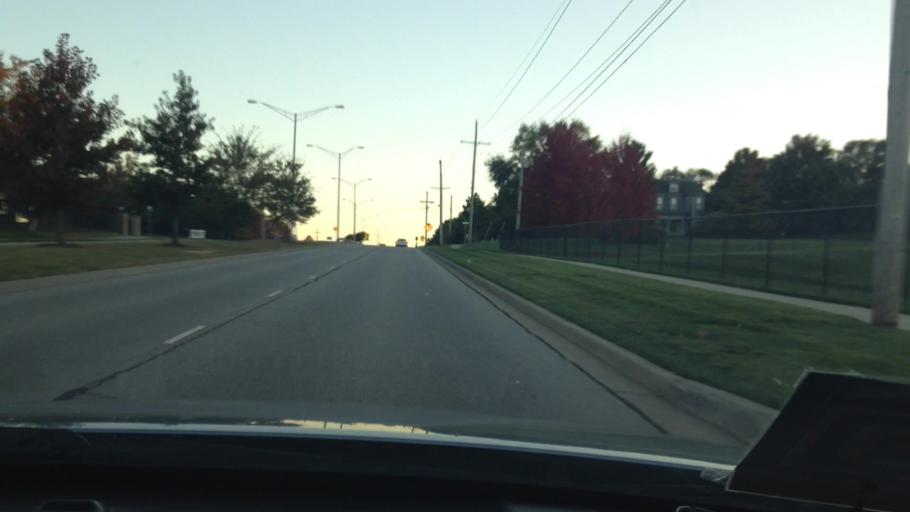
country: US
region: Kansas
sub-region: Johnson County
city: Lenexa
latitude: 38.8746
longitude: -94.7006
